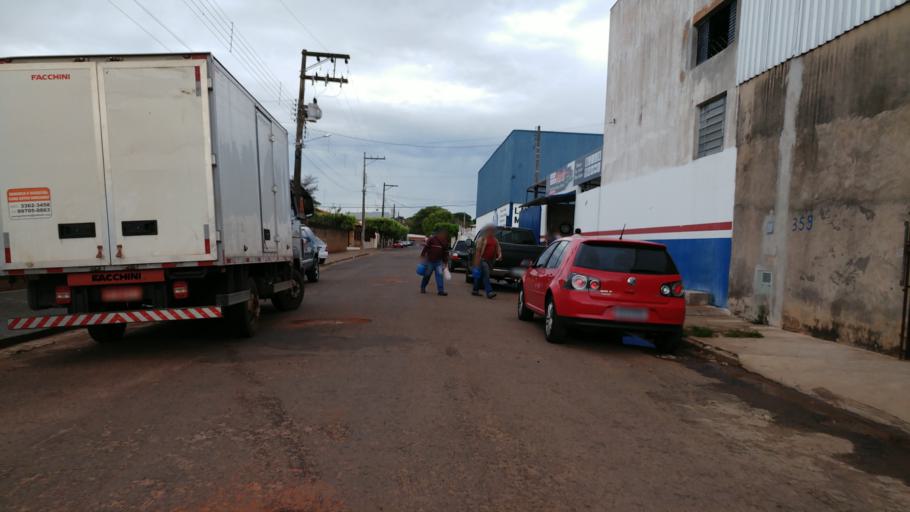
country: BR
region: Sao Paulo
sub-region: Paraguacu Paulista
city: Paraguacu Paulista
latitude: -22.4242
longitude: -50.5832
